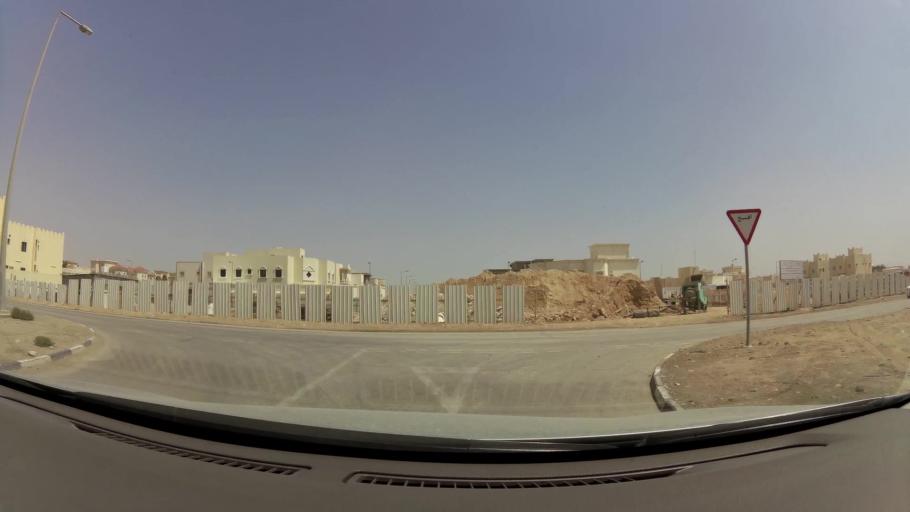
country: QA
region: Baladiyat Umm Salal
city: Umm Salal Muhammad
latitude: 25.4006
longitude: 51.4379
